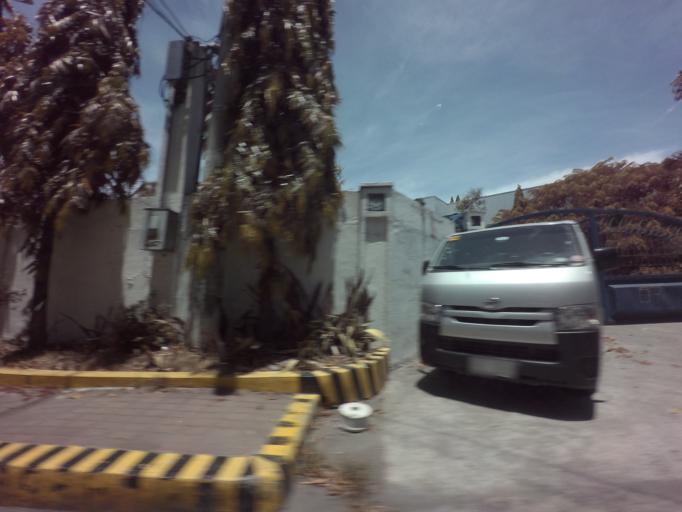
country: PH
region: Metro Manila
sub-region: Makati City
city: Makati City
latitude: 14.5064
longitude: 121.0268
